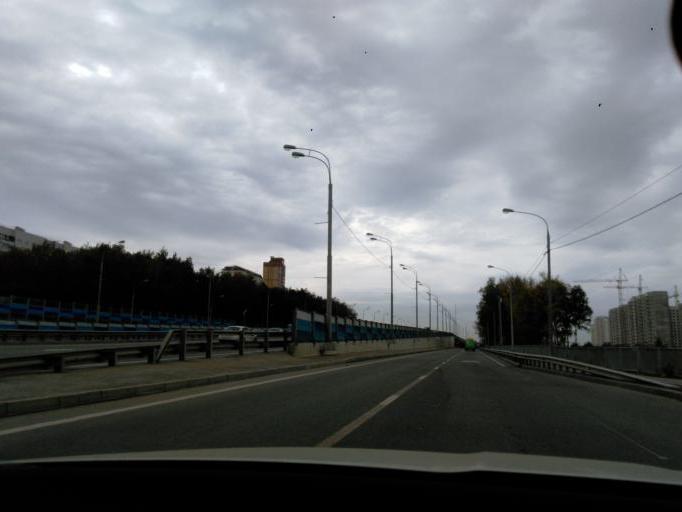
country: RU
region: Moscow
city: Severnyy
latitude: 55.9361
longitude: 37.5460
